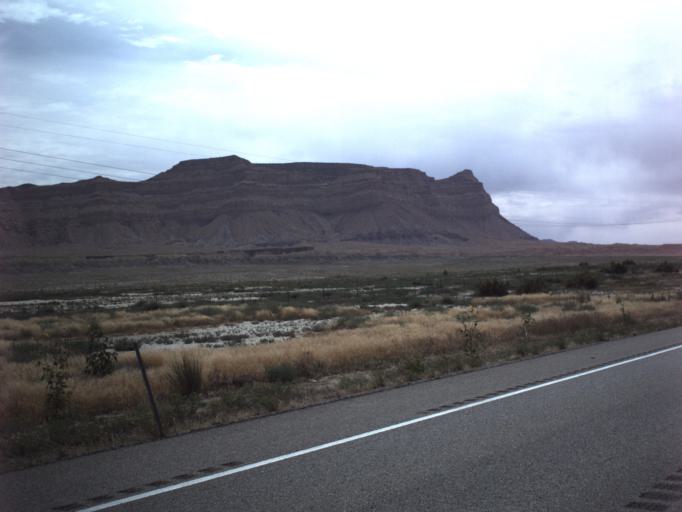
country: US
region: Utah
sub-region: Carbon County
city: East Carbon City
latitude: 39.2358
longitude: -110.3388
